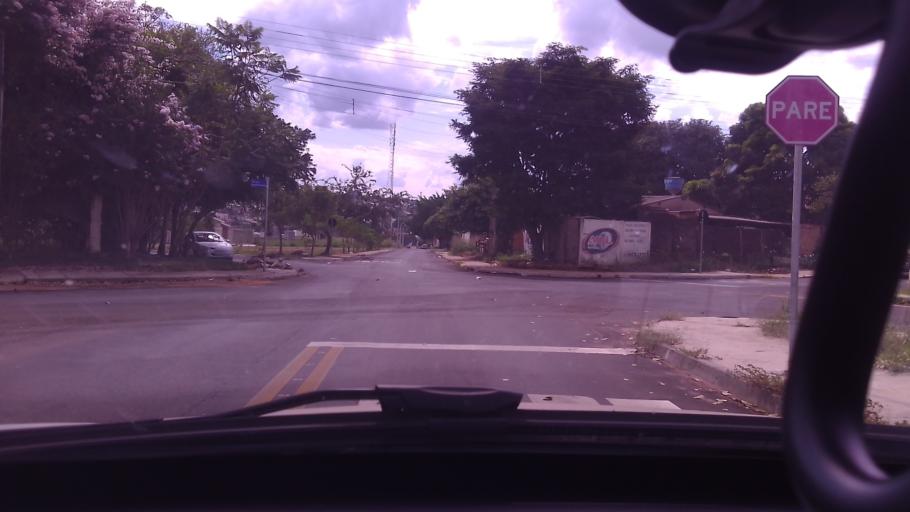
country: BR
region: Goias
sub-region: Mineiros
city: Mineiros
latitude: -17.5786
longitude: -52.5523
